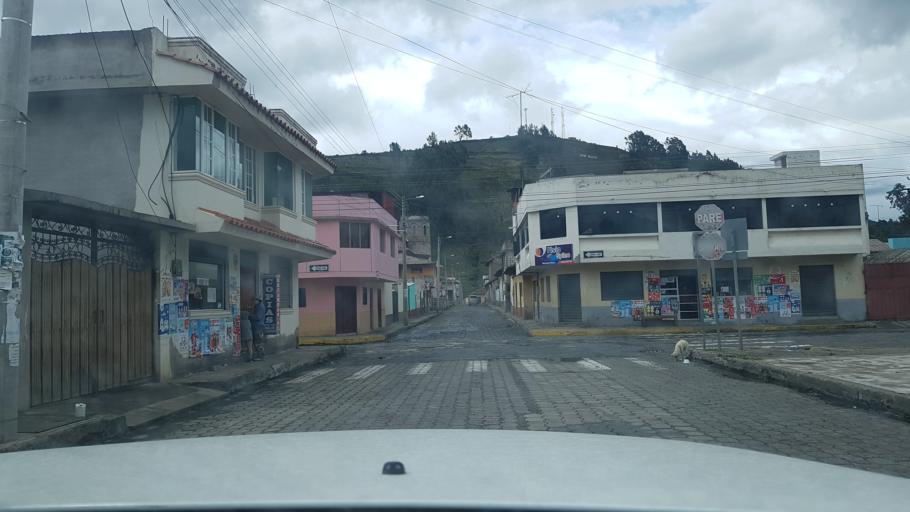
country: EC
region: Chimborazo
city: Riobamba
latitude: -1.7037
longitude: -78.7746
